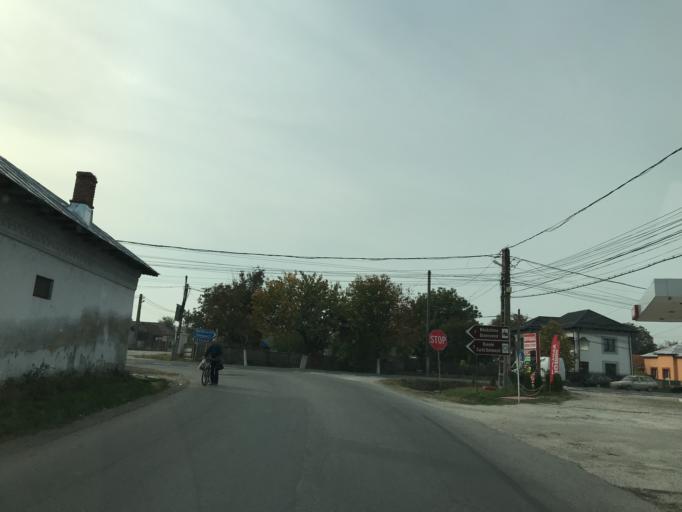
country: RO
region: Olt
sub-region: Comuna Piatra Olt
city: Piatra
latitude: 44.3649
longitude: 24.2930
